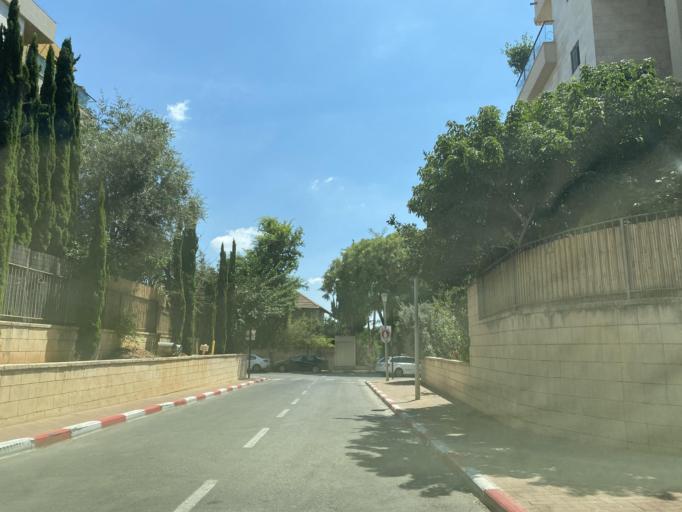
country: IL
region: Central District
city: Ra'anana
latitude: 32.1850
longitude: 34.8877
